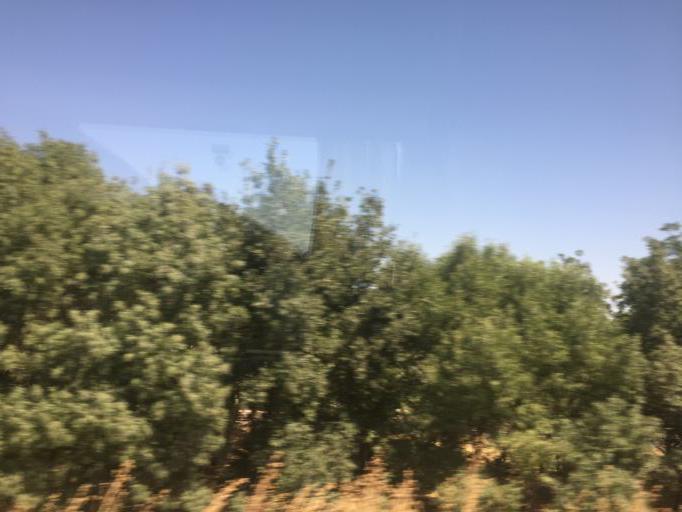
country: TR
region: Diyarbakir
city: Tepe
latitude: 37.8479
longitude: 40.8027
